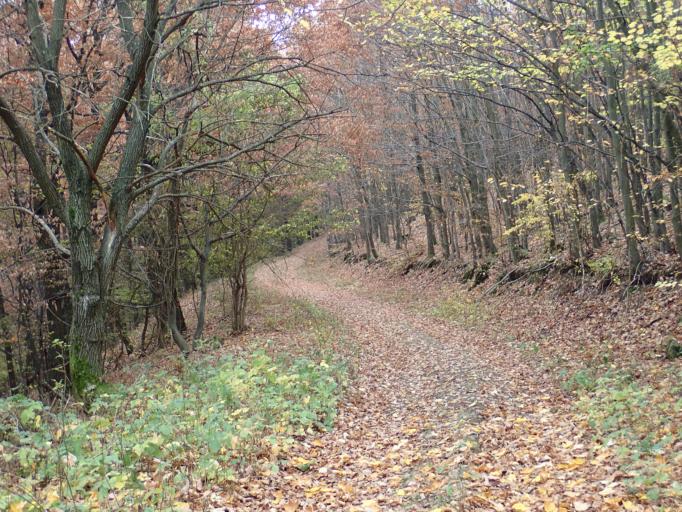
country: HU
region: Borsod-Abauj-Zemplen
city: Bogacs
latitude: 47.9744
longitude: 20.5152
